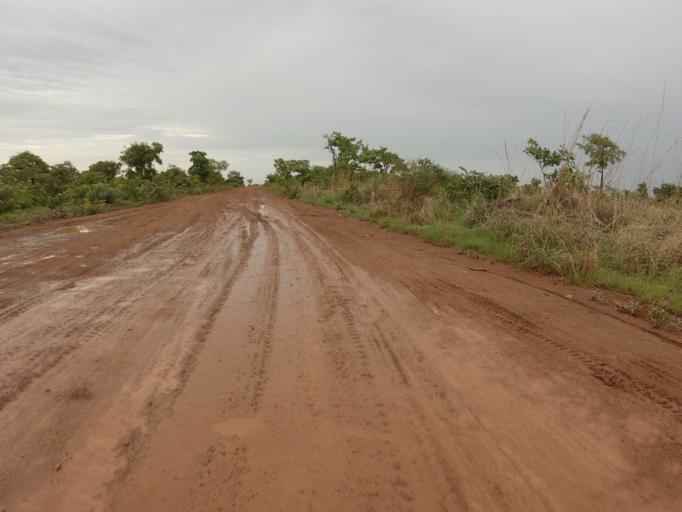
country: GH
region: Upper East
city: Bolgatanga
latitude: 10.8782
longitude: -0.6300
